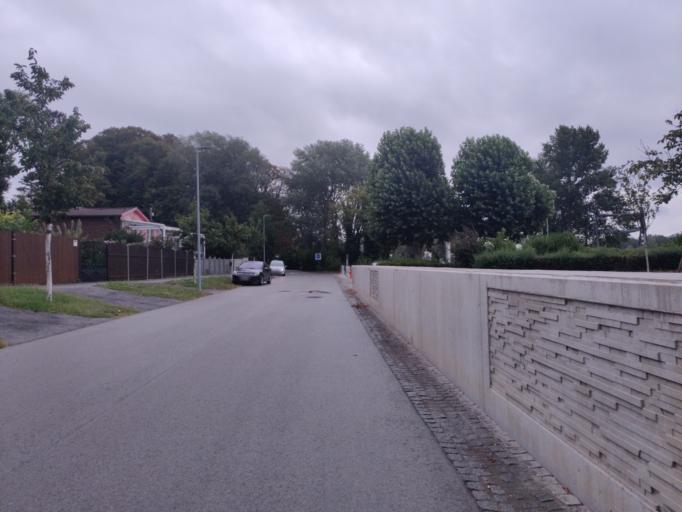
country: AT
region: Lower Austria
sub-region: Politischer Bezirk Korneuburg
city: Korneuburg
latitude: 48.3381
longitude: 16.3224
